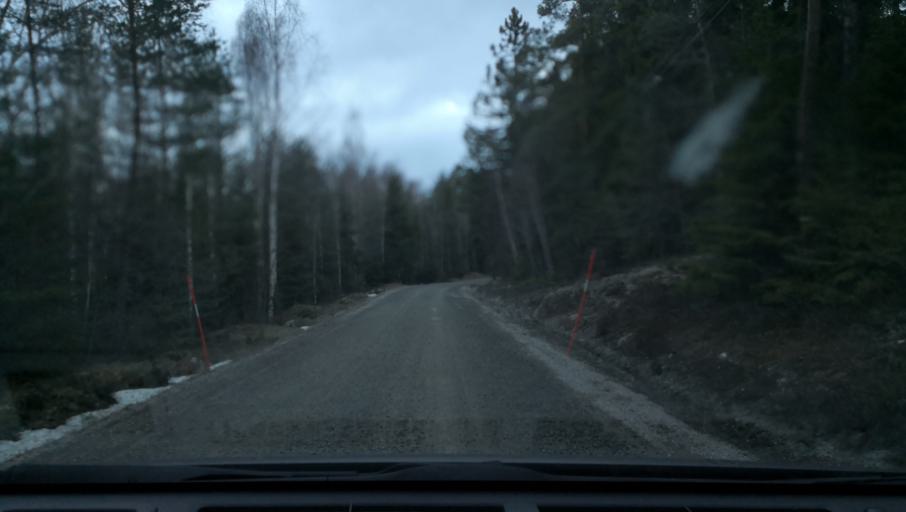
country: SE
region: Vaestmanland
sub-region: Kopings Kommun
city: Kolsva
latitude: 59.5755
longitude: 15.7131
